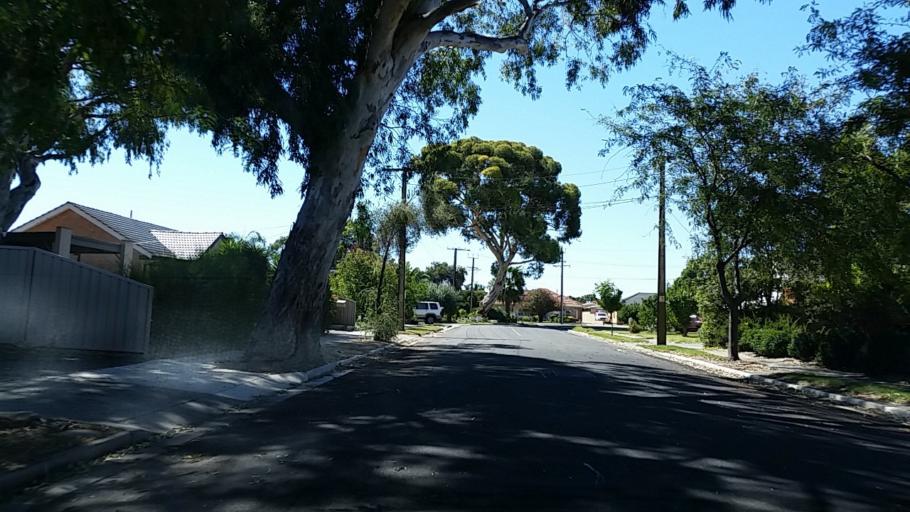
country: AU
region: South Australia
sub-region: Charles Sturt
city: Henley Beach
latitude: -34.9241
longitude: 138.5094
